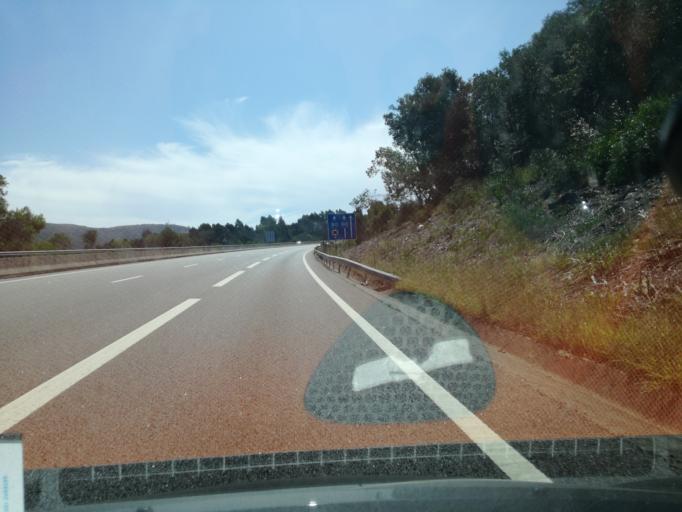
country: PT
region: Viana do Castelo
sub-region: Caminha
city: Vila Praia de Ancora
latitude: 41.7964
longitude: -8.7946
